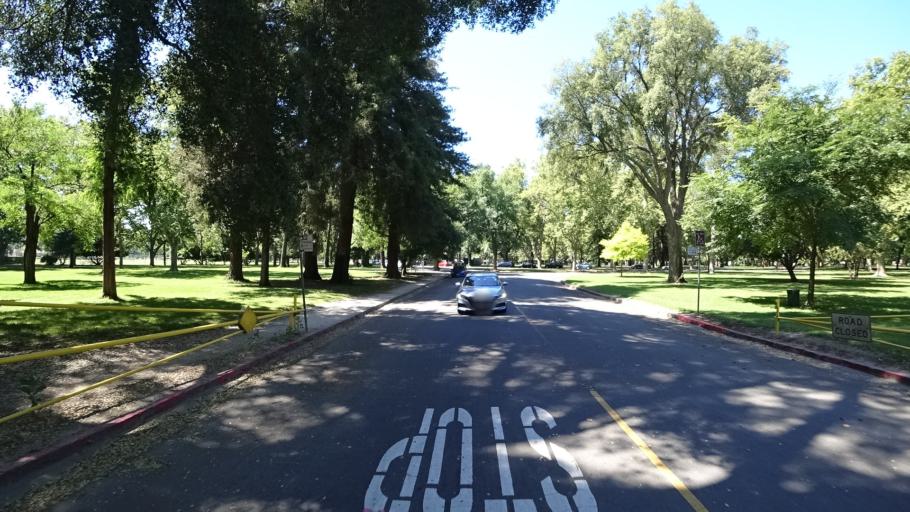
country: US
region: California
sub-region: Sacramento County
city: Sacramento
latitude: 38.5461
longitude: -121.5030
